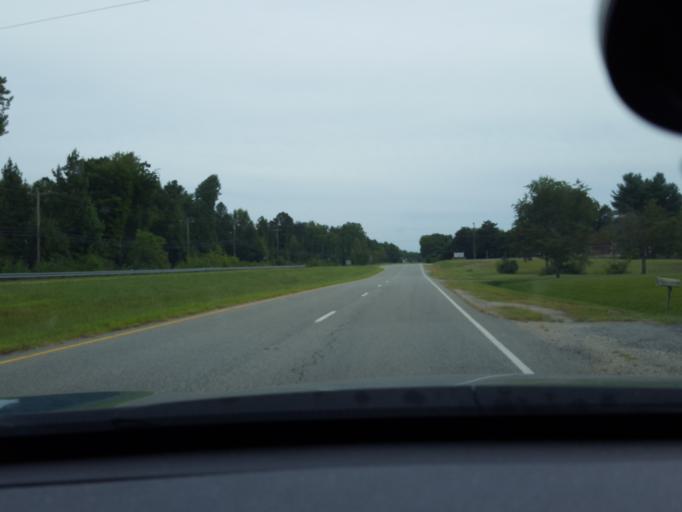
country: US
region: Virginia
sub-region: Caroline County
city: Bowling Green
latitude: 38.0335
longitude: -77.3417
